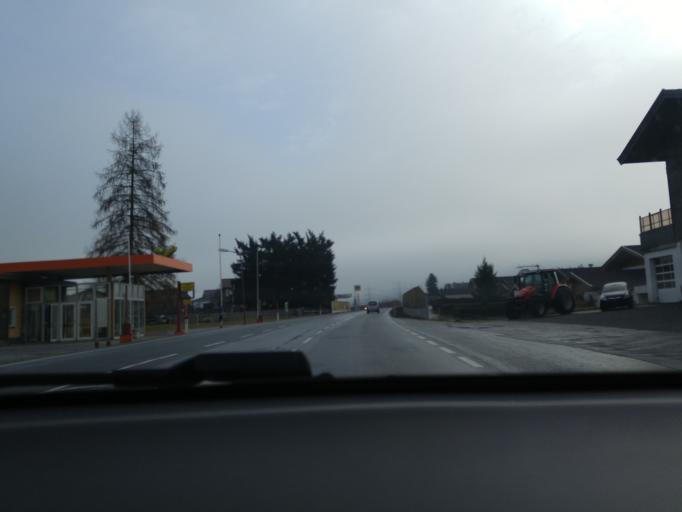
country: AT
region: Salzburg
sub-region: Politischer Bezirk Zell am See
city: Niedernsill
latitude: 47.2842
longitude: 12.6213
